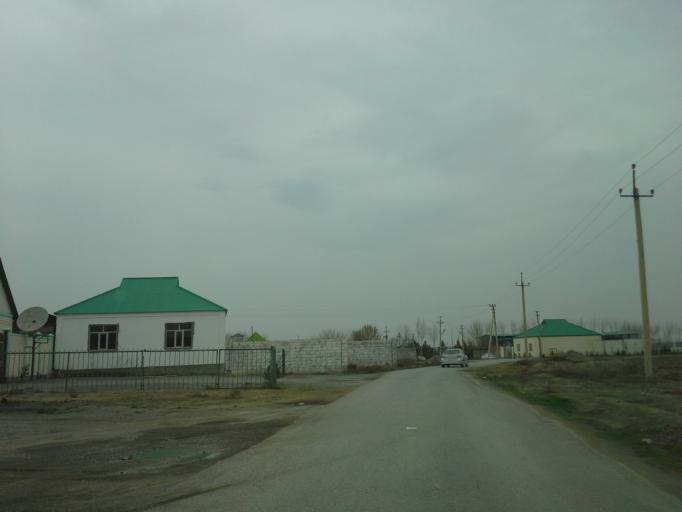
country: TM
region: Ahal
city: Abadan
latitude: 37.9733
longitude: 58.2296
